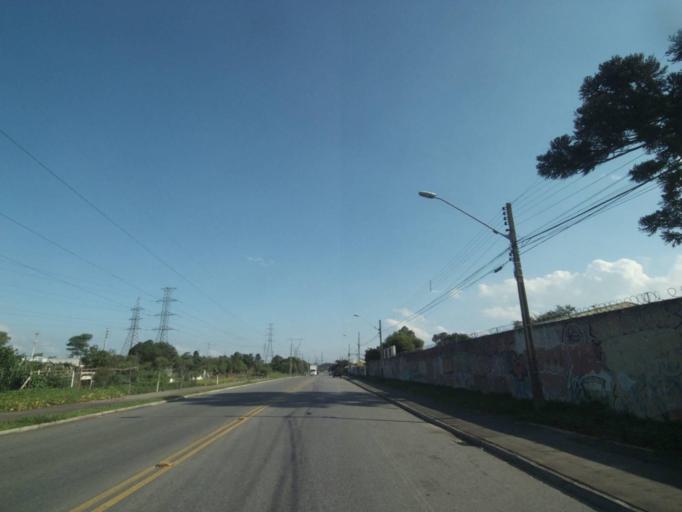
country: BR
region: Parana
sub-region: Araucaria
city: Araucaria
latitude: -25.5269
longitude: -49.3336
